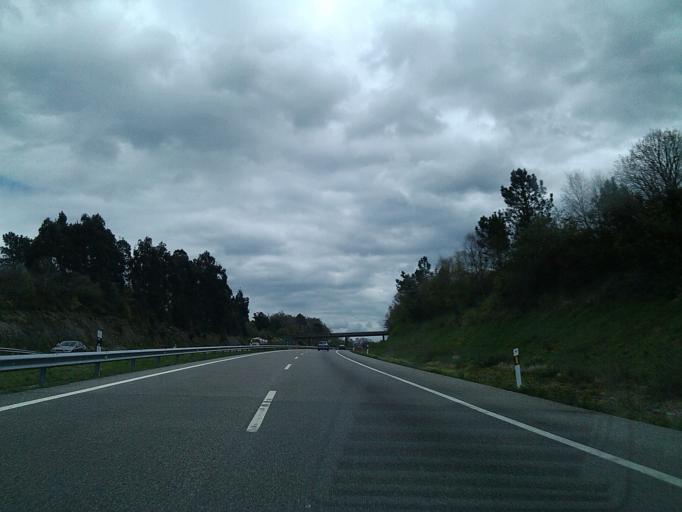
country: ES
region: Galicia
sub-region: Provincia de Lugo
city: Guitiriz
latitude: 43.1926
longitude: -7.8734
